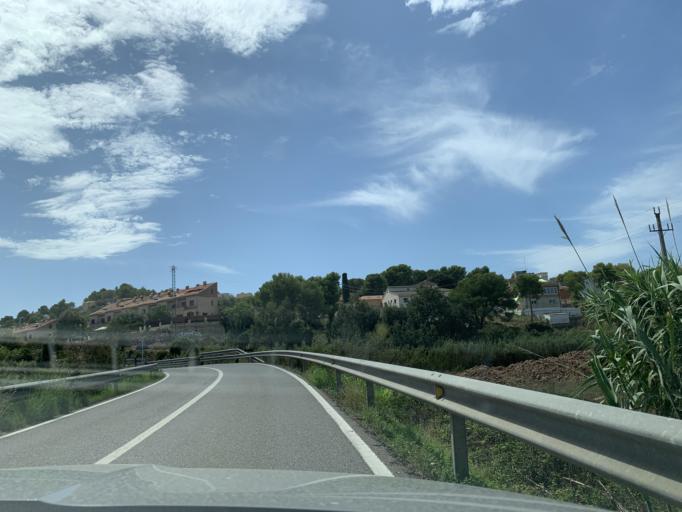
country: ES
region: Catalonia
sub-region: Provincia de Tarragona
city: Altafulla
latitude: 41.1591
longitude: 1.3630
